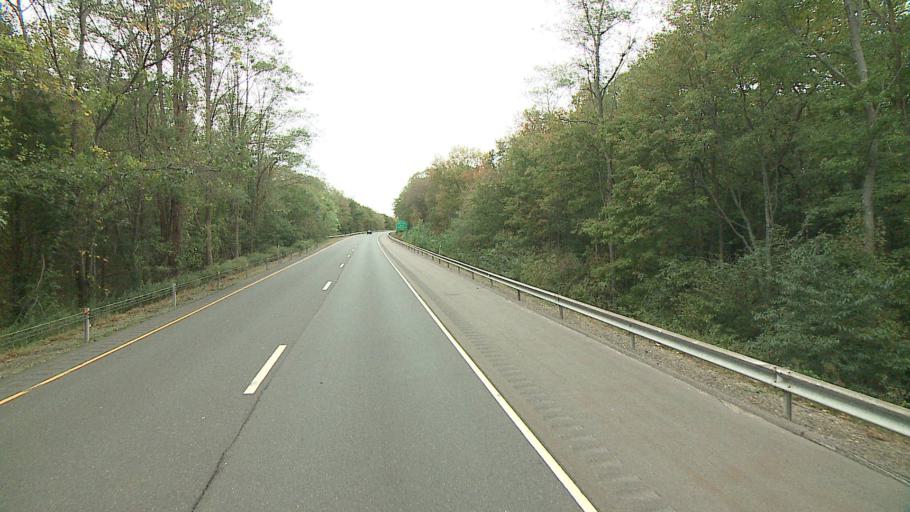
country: US
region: Connecticut
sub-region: Middlesex County
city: Essex Village
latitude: 41.3341
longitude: -72.3925
